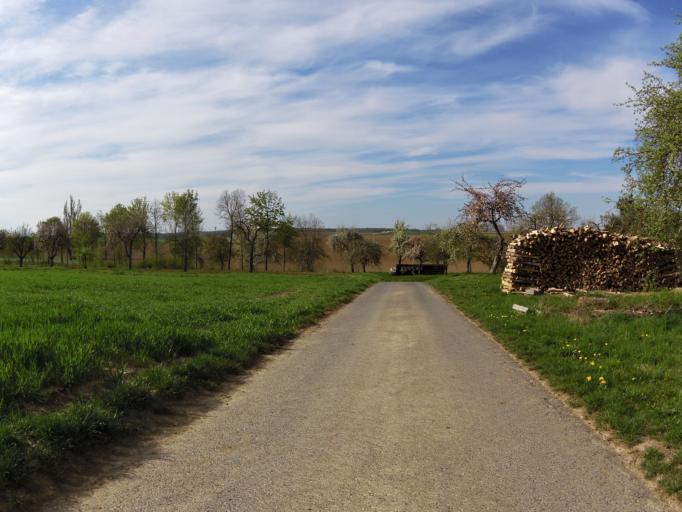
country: DE
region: Bavaria
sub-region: Regierungsbezirk Unterfranken
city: Unterpleichfeld
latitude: 49.8722
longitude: 10.0240
